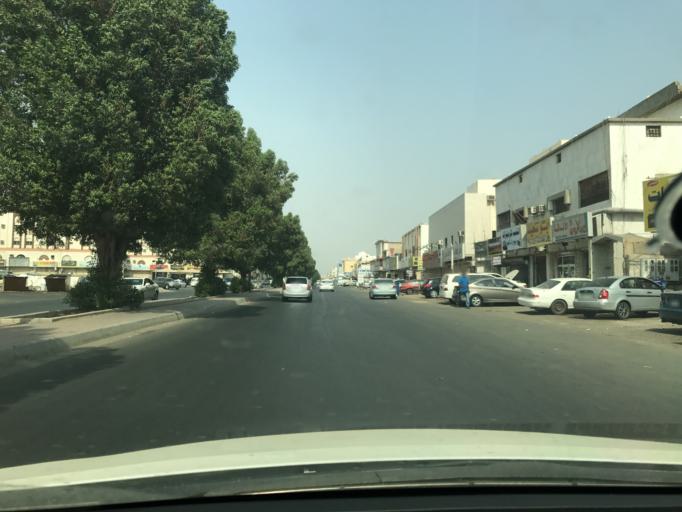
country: SA
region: Makkah
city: Jeddah
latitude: 21.6204
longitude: 39.1689
